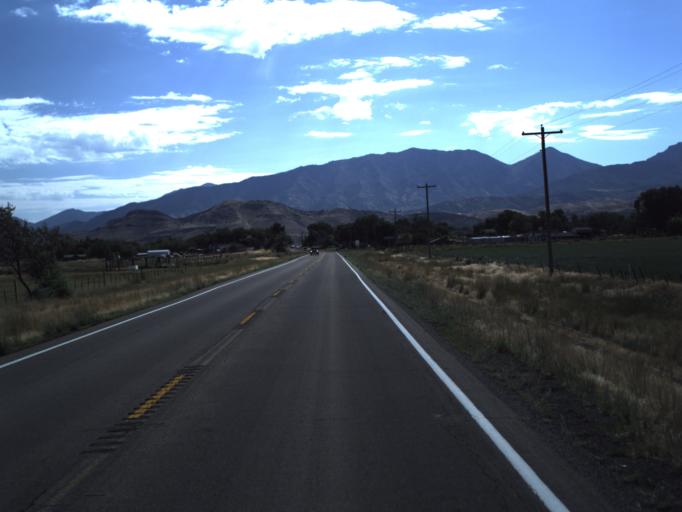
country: US
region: Utah
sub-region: Utah County
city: Genola
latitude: 39.9525
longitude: -111.9113
